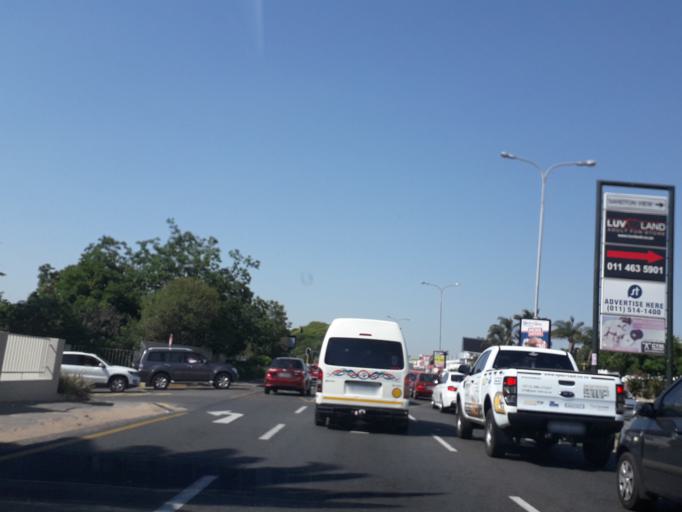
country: ZA
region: Gauteng
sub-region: City of Johannesburg Metropolitan Municipality
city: Johannesburg
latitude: -26.0767
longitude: 28.0116
